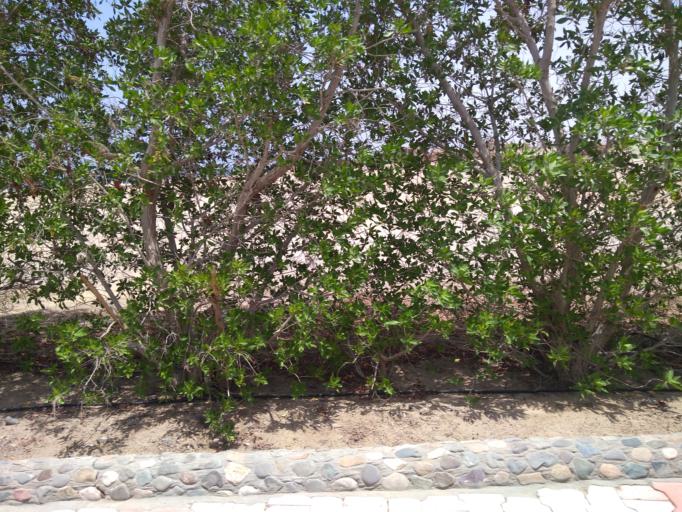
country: EG
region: Red Sea
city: Al Qusayr
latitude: 25.9133
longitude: 34.4062
